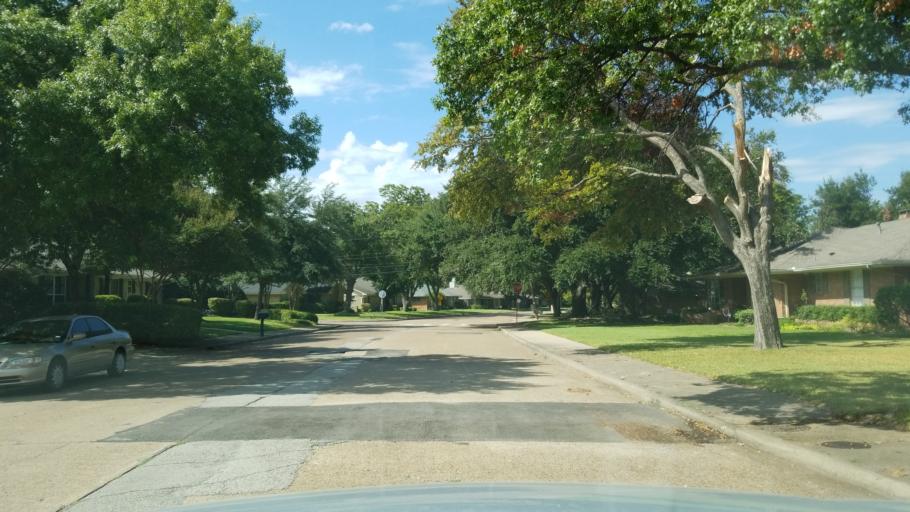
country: US
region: Texas
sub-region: Dallas County
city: Richardson
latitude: 32.9563
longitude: -96.7719
